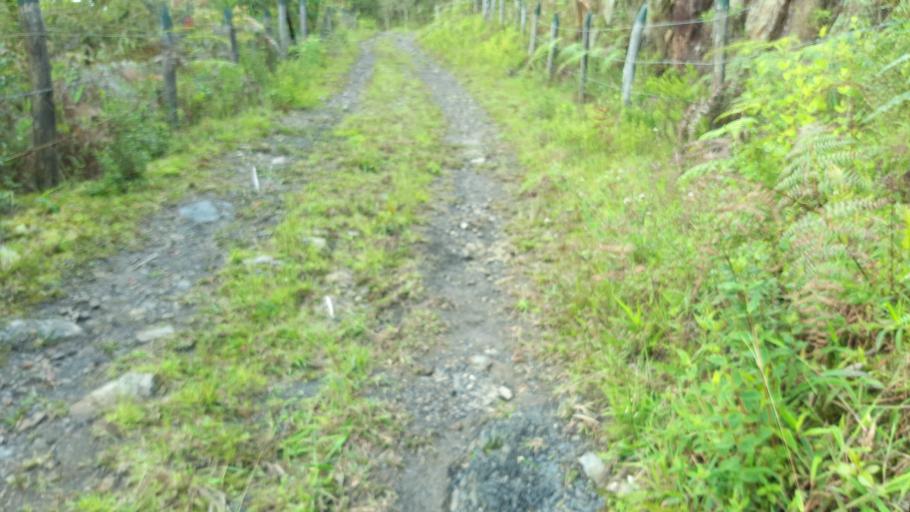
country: CO
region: Boyaca
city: Garagoa
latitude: 5.0854
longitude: -73.3176
